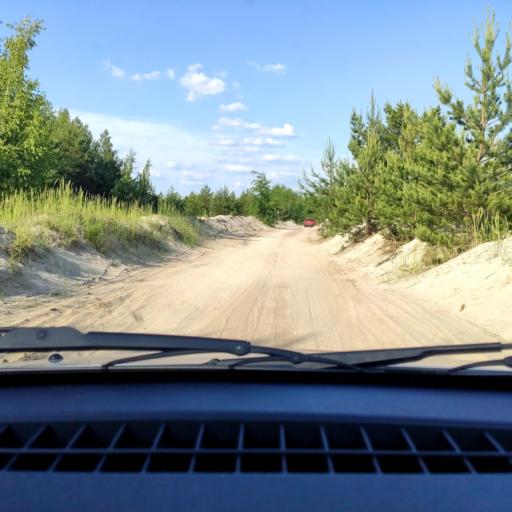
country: RU
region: Voronezj
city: Somovo
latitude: 51.7773
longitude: 39.2906
